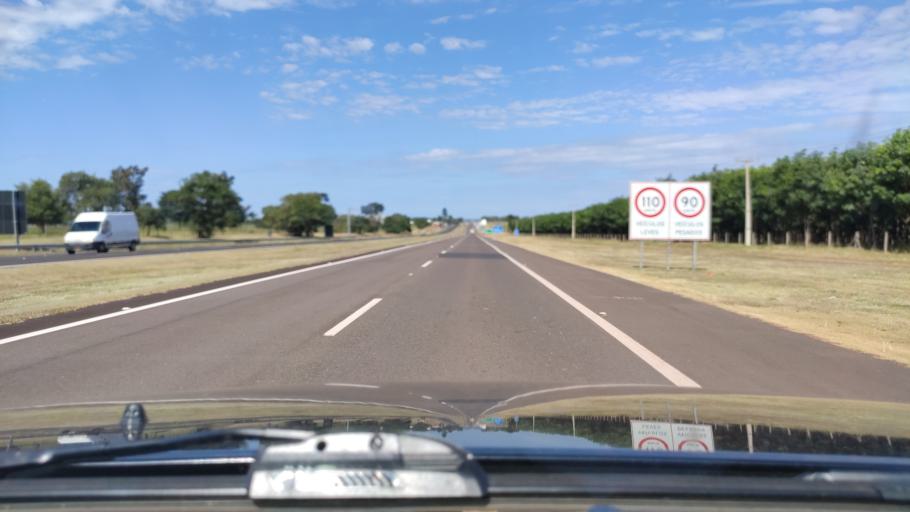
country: BR
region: Sao Paulo
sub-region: Rancharia
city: Rancharia
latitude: -22.4454
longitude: -50.9913
